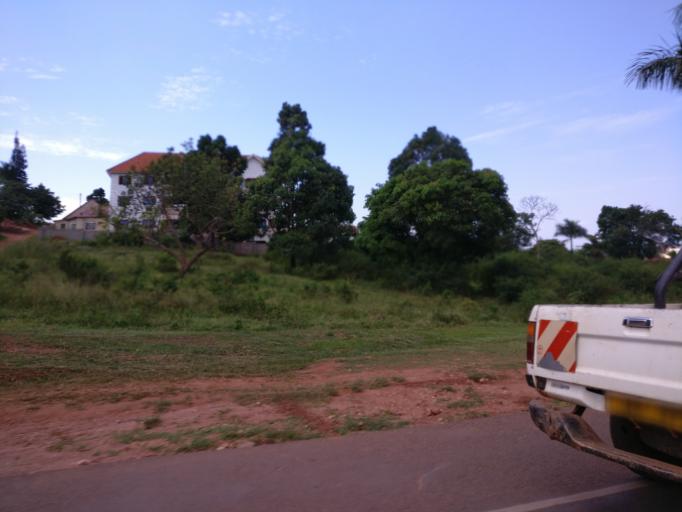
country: UG
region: Central Region
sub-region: Wakiso District
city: Kajansi
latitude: 0.1567
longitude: 32.5458
